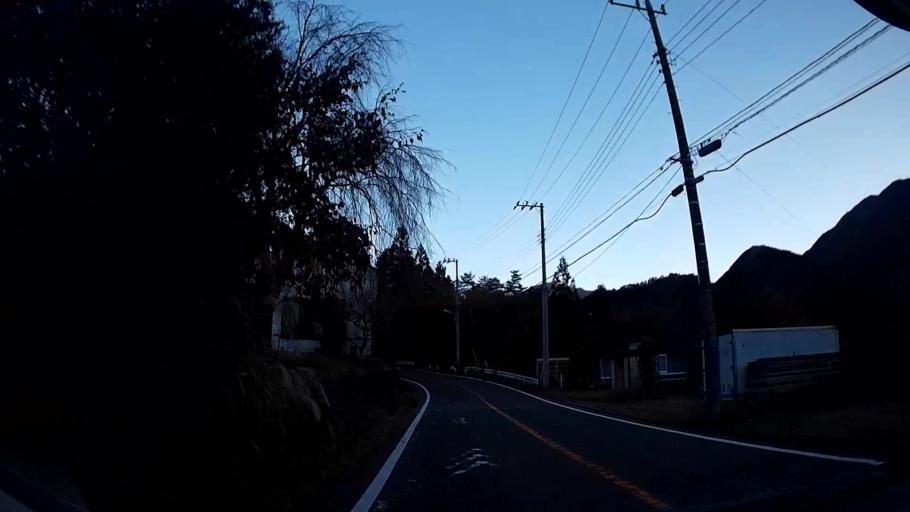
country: JP
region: Yamanashi
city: Uenohara
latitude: 35.5294
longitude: 139.0967
